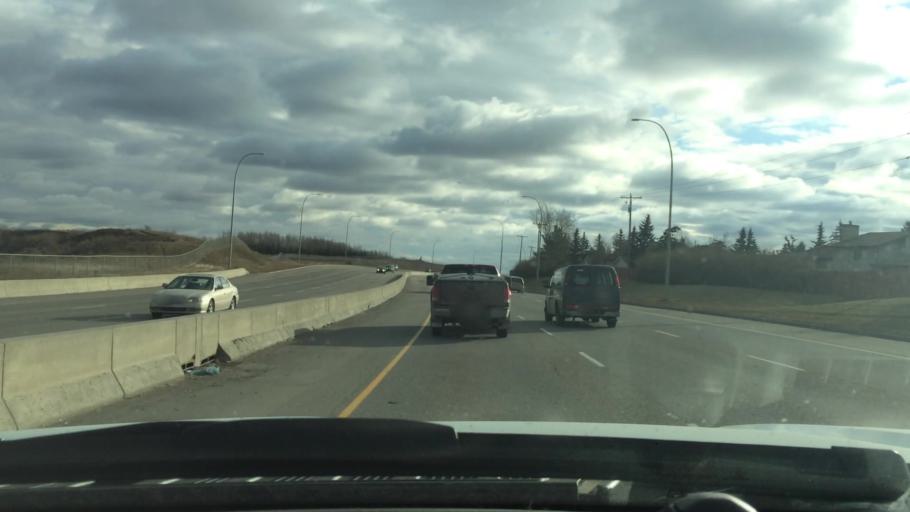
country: CA
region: Alberta
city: Calgary
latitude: 51.1311
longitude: -114.0620
